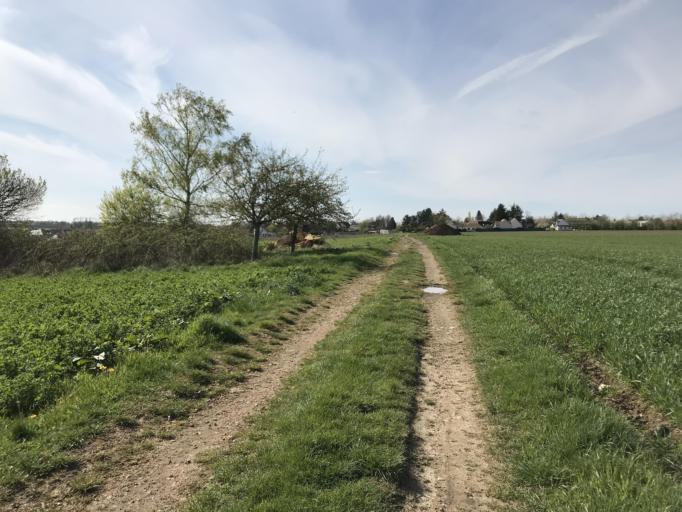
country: FR
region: Ile-de-France
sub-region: Departement de l'Essonne
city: Gometz-la-Ville
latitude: 48.6682
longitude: 2.1348
